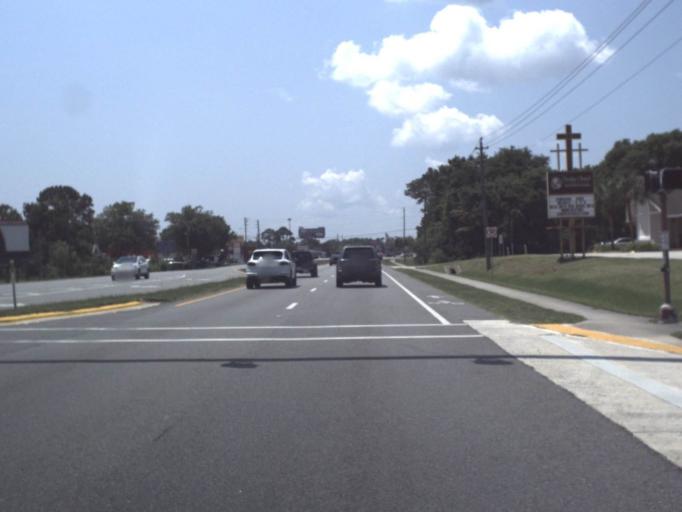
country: US
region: Florida
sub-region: Saint Johns County
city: Saint Augustine
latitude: 29.8754
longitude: -81.3240
